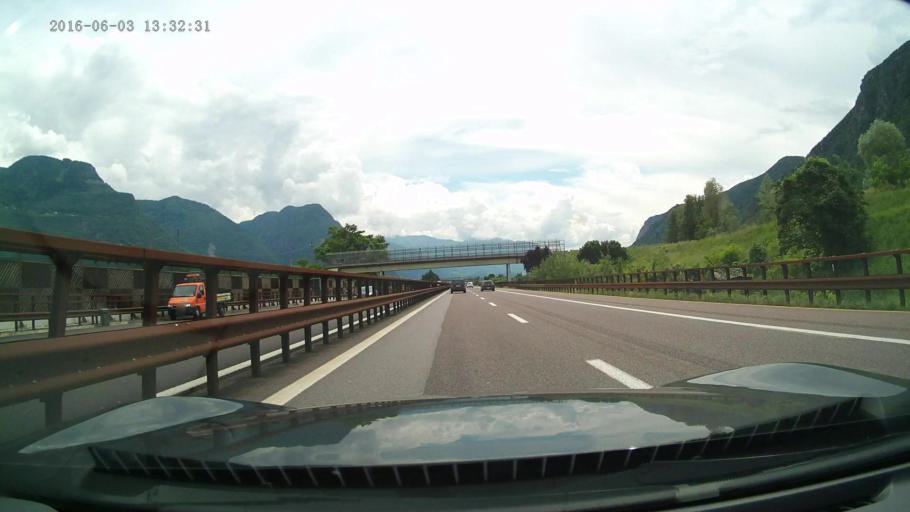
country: IT
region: Trentino-Alto Adige
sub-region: Bolzano
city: Laives
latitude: 46.4341
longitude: 11.3168
